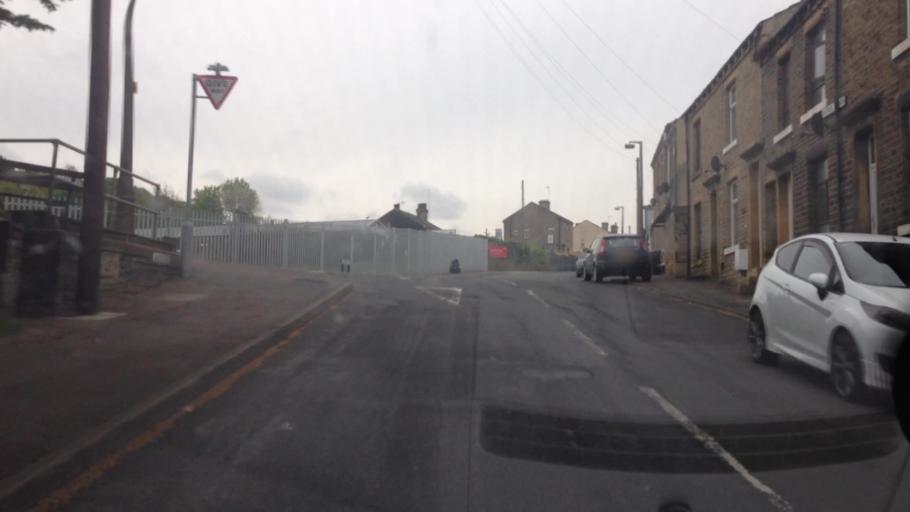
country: GB
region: England
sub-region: Calderdale
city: Brighouse
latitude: 53.6970
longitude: -1.7839
